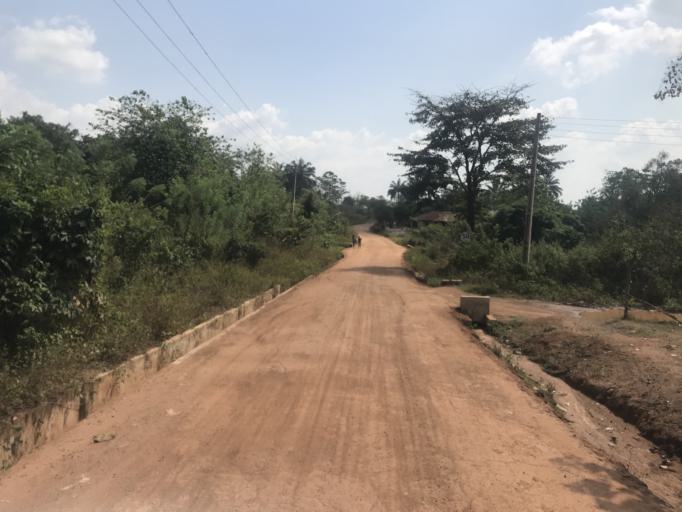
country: NG
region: Osun
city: Iragbiji
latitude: 7.8910
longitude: 4.7014
